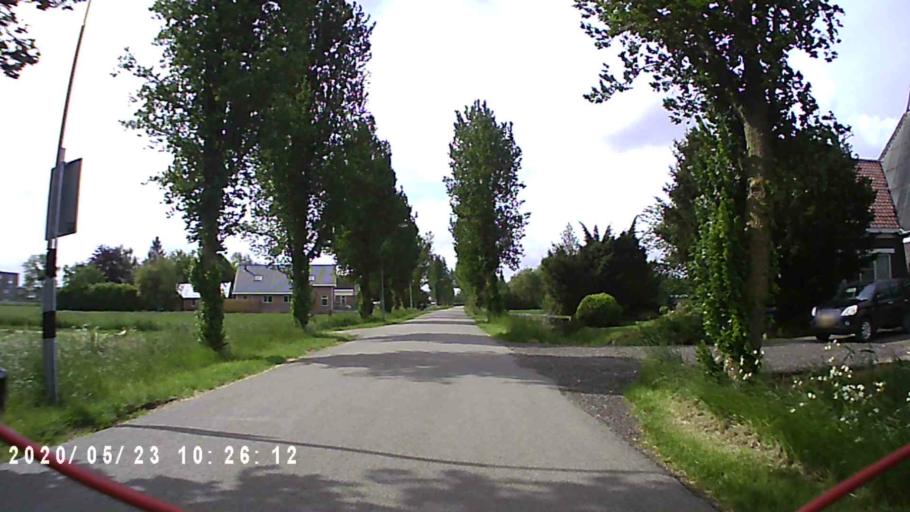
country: NL
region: Groningen
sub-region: Gemeente Appingedam
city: Appingedam
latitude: 53.3045
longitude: 6.8523
